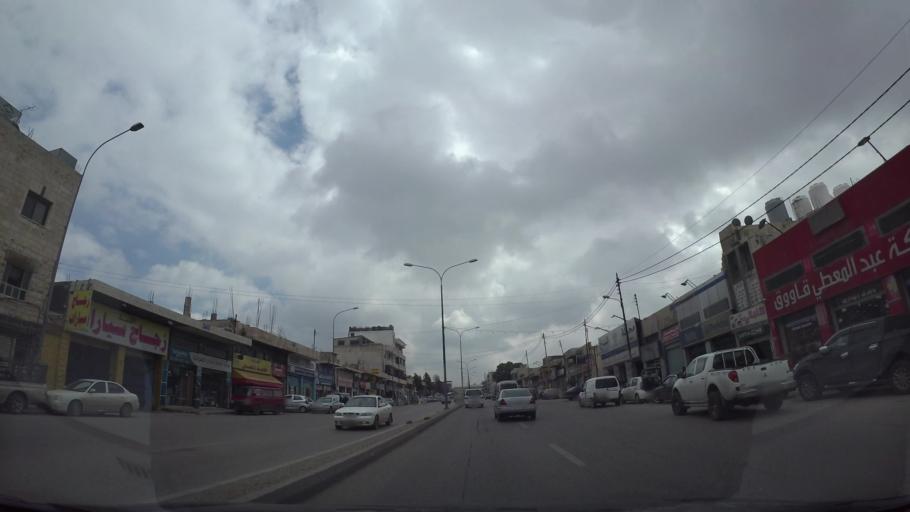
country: JO
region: Amman
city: Al Quwaysimah
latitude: 31.9176
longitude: 35.9385
